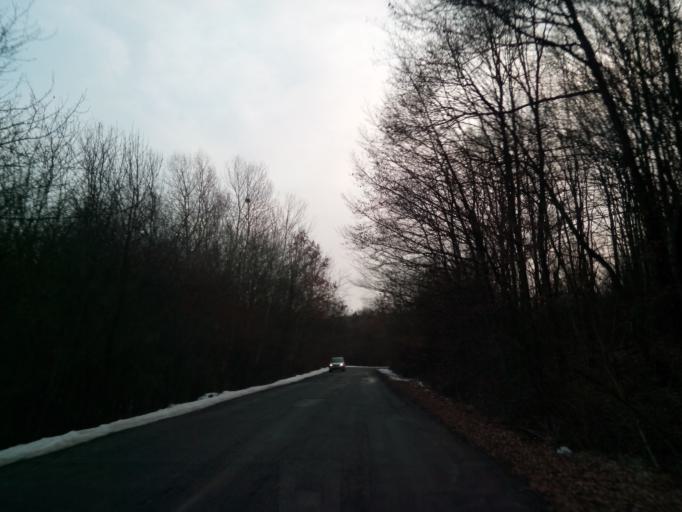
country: HU
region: Borsod-Abauj-Zemplen
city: Gonc
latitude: 48.4857
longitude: 21.3960
